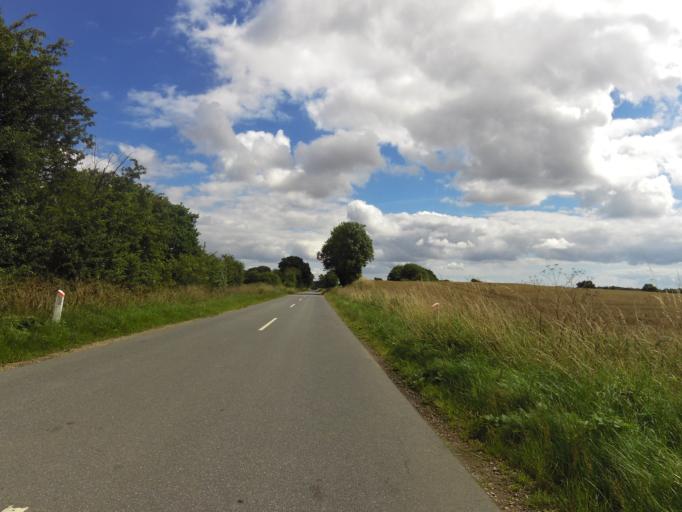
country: DK
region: South Denmark
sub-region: Haderslev Kommune
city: Vojens
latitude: 55.2840
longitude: 9.3783
